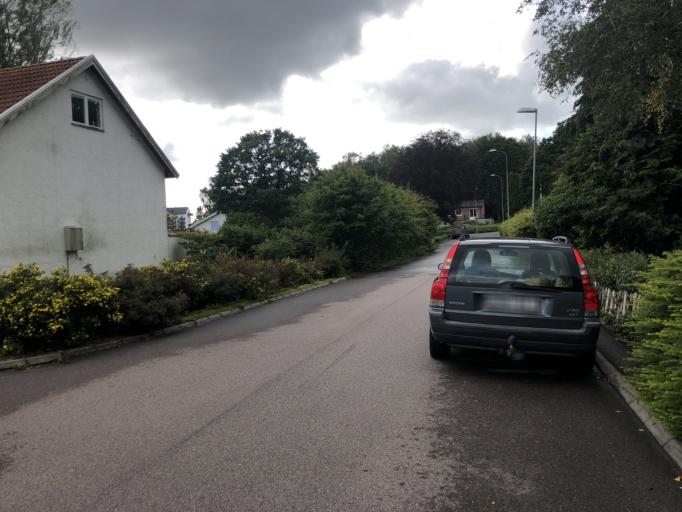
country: SE
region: Vaestra Goetaland
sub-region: Goteborg
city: Goeteborg
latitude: 57.7558
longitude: 11.9348
